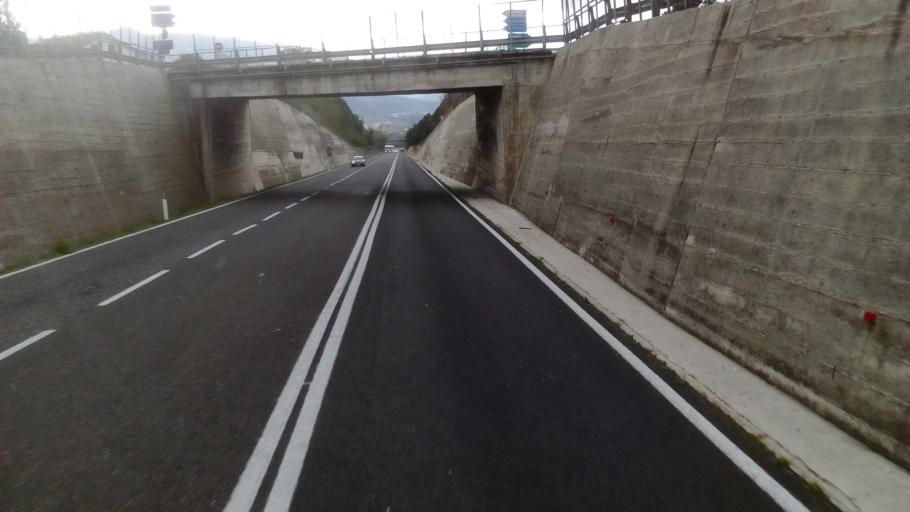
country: IT
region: Molise
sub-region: Provincia di Isernia
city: Isernia
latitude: 41.5897
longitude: 14.2398
